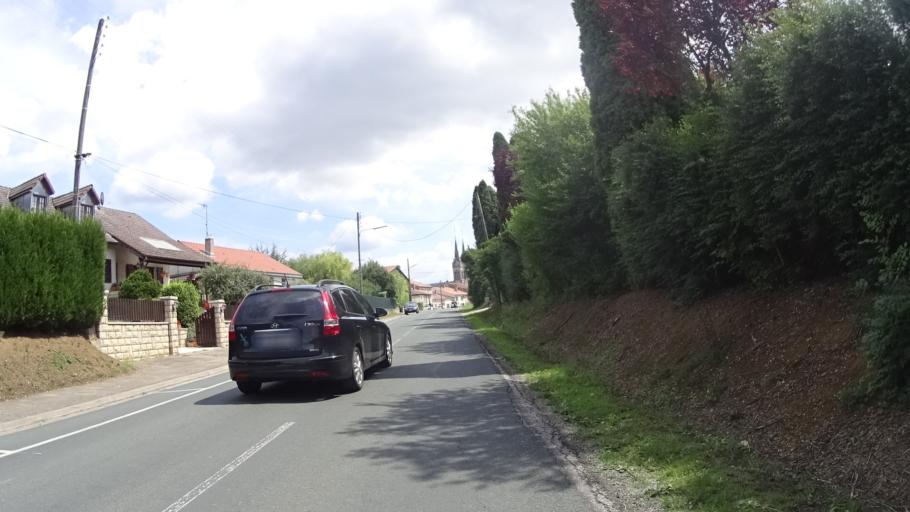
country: FR
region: Lorraine
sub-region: Departement de la Meuse
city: Euville
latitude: 48.7518
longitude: 5.6218
